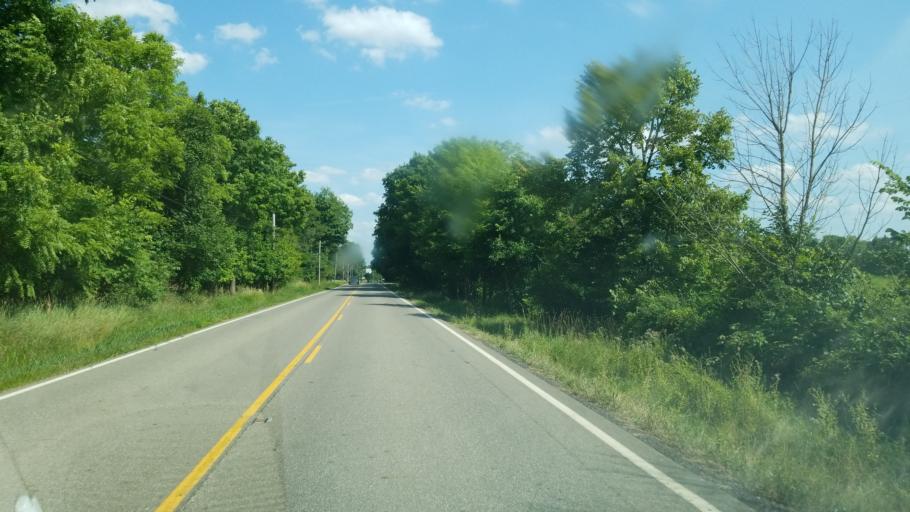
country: US
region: Ohio
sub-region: Huron County
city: Greenwich
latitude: 40.9482
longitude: -82.5642
